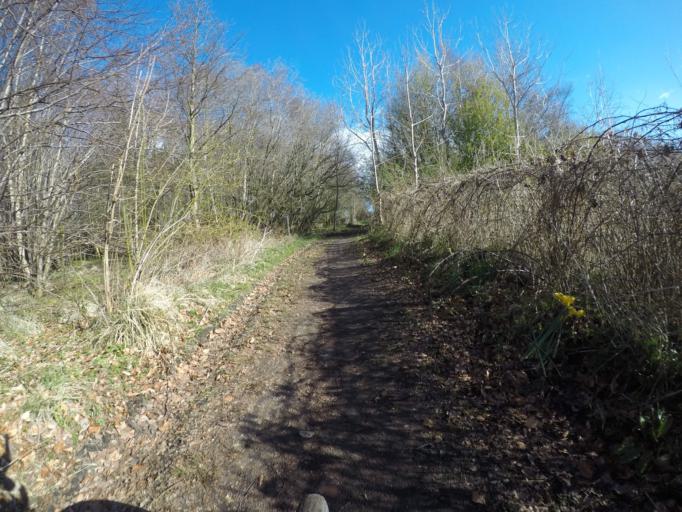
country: GB
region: Scotland
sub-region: North Ayrshire
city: Irvine
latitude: 55.6482
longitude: -4.6596
